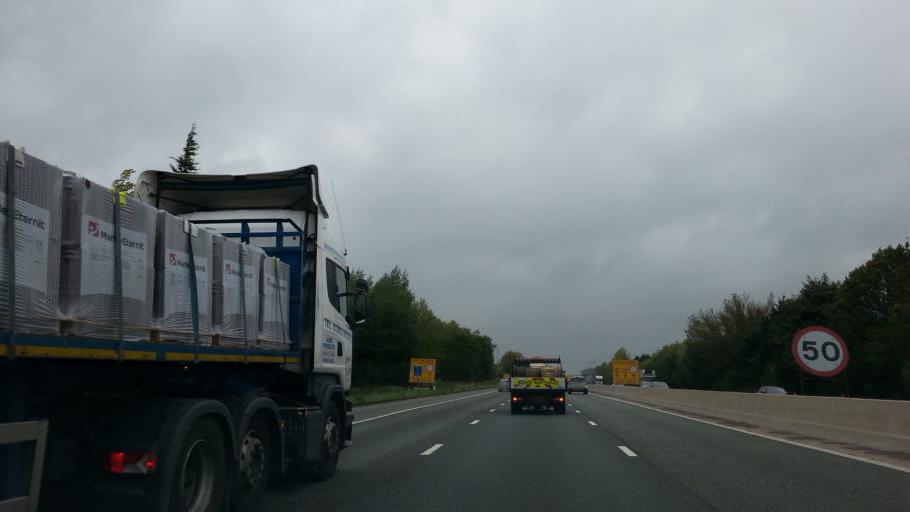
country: GB
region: England
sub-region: Warrington
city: Lymm
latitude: 53.3379
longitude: -2.4862
